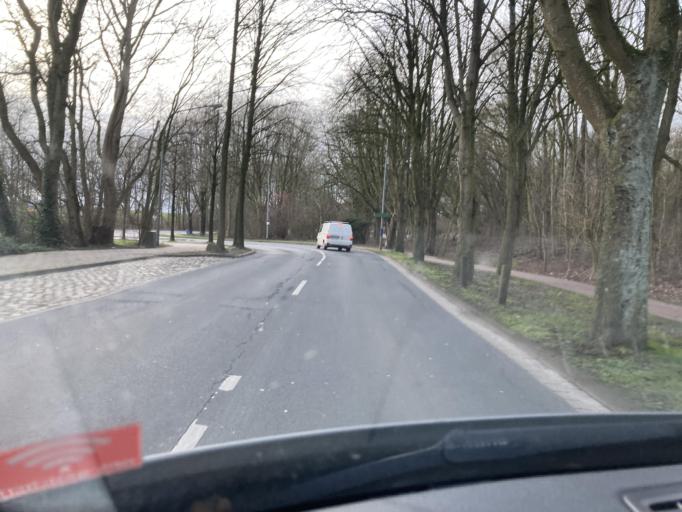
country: DE
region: Lower Saxony
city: Leer
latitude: 53.2161
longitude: 7.4399
